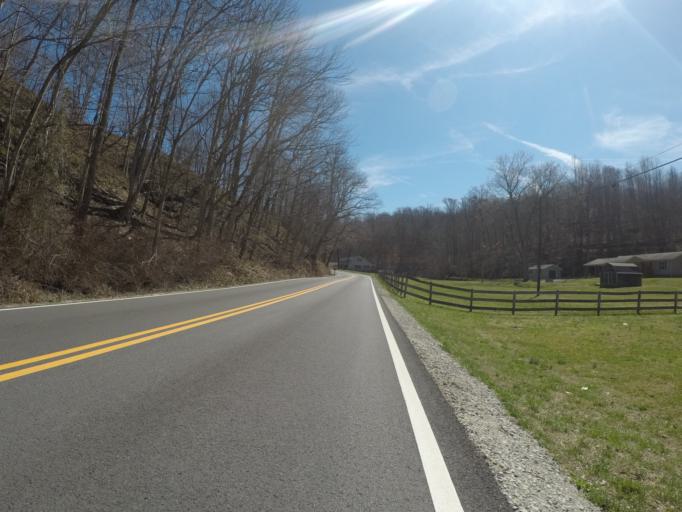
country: US
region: Ohio
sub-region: Lawrence County
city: South Point
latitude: 38.4632
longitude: -82.5598
